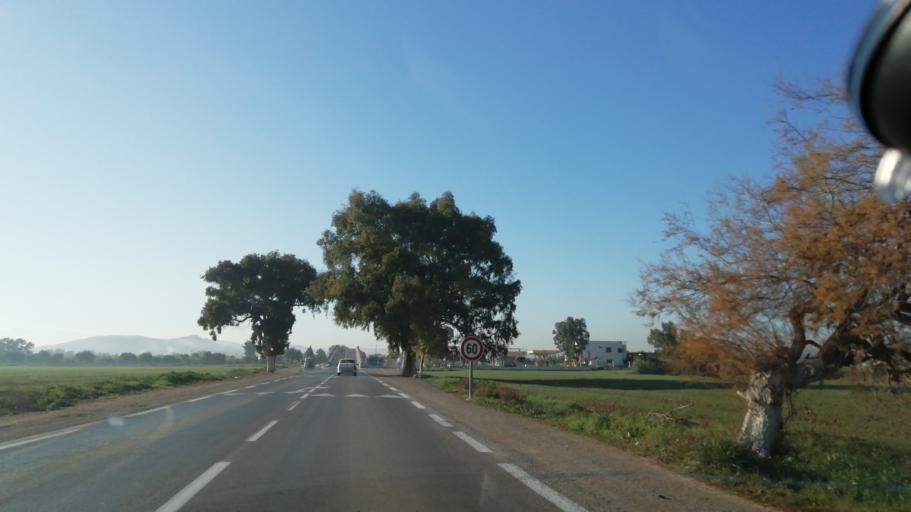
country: DZ
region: Tlemcen
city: Remchi
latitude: 35.0500
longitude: -1.5028
